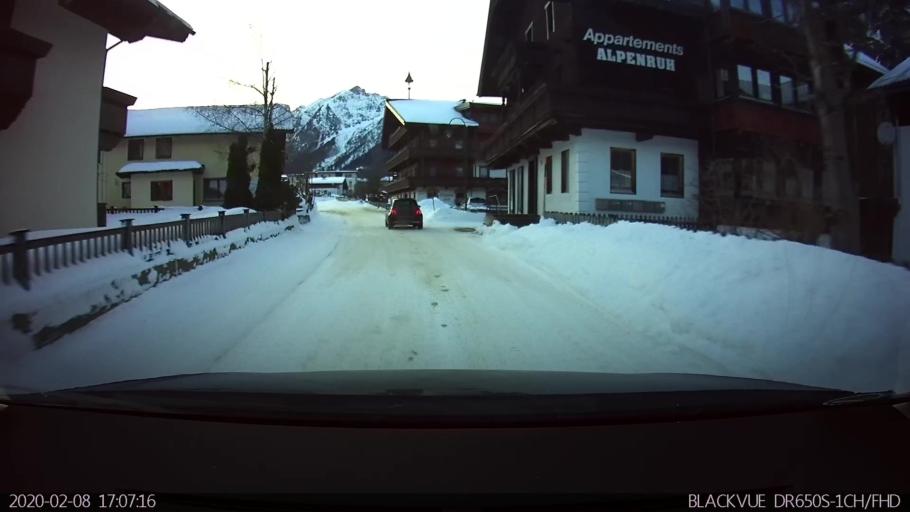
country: AT
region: Tyrol
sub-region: Politischer Bezirk Schwaz
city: Stans
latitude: 47.4409
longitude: 11.6929
